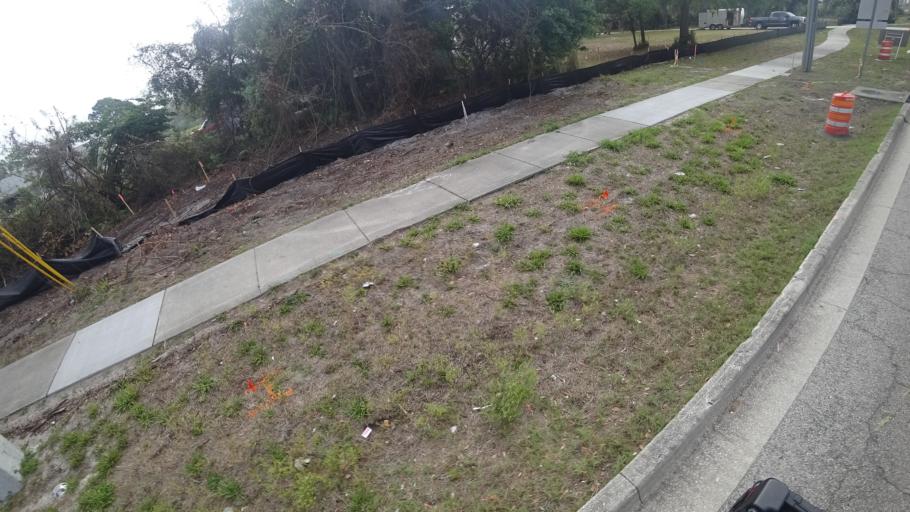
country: US
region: Florida
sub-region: Manatee County
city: Samoset
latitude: 27.4480
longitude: -82.5056
